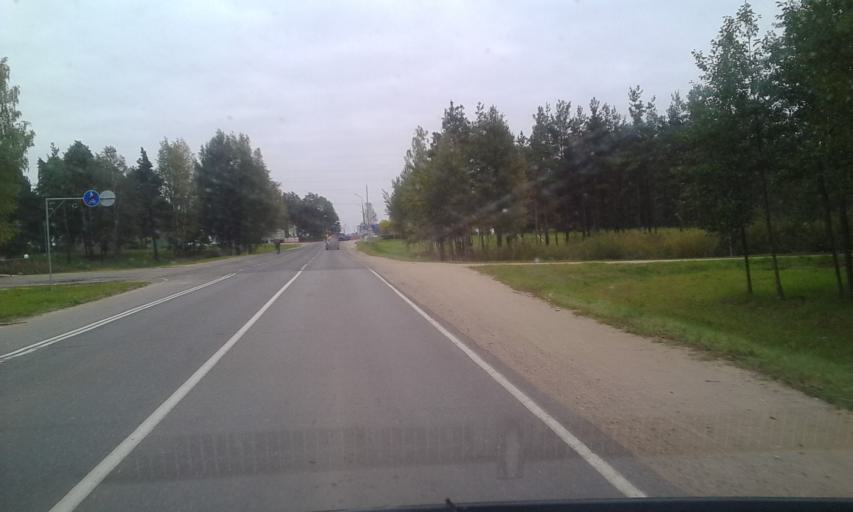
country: BY
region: Vitebsk
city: Pastavy
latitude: 55.1151
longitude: 26.8720
